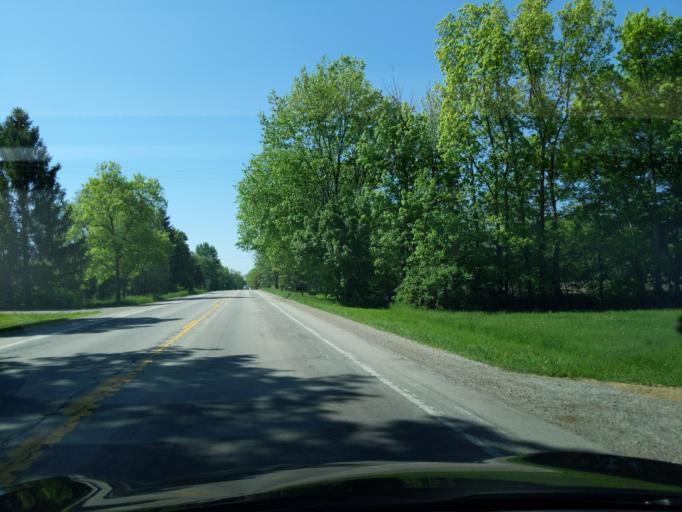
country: US
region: Michigan
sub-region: Ingham County
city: Stockbridge
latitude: 42.4837
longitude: -84.1901
